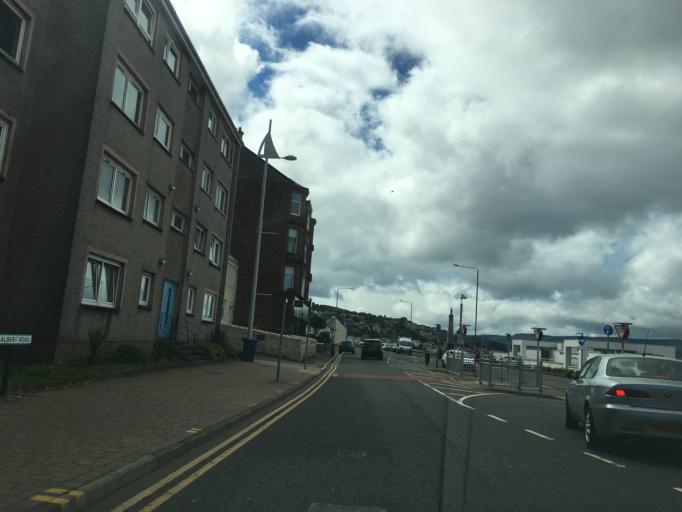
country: GB
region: Scotland
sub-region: Inverclyde
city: Gourock
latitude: 55.9613
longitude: -4.8210
